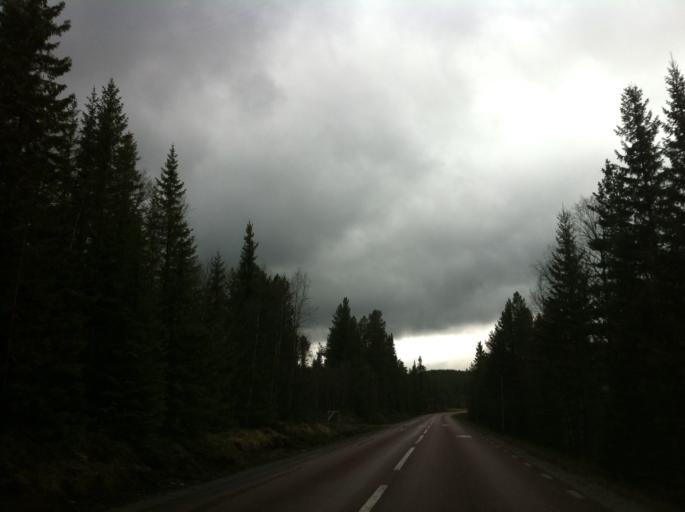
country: NO
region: Hedmark
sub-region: Engerdal
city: Engerdal
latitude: 62.4321
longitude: 12.7149
